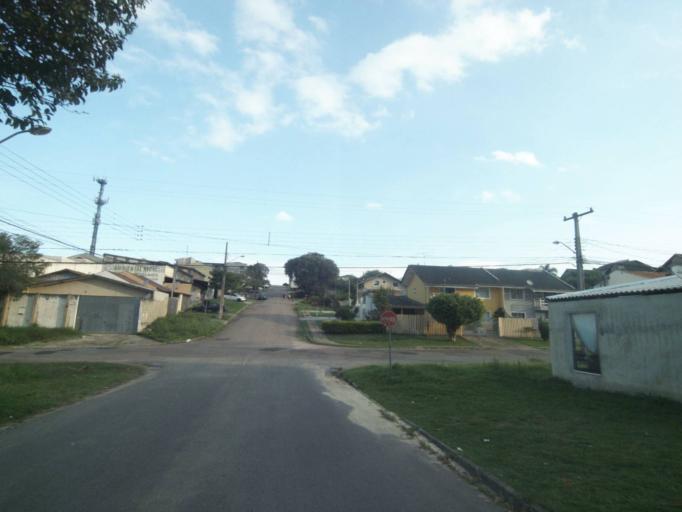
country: BR
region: Parana
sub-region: Pinhais
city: Pinhais
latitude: -25.3992
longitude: -49.2048
